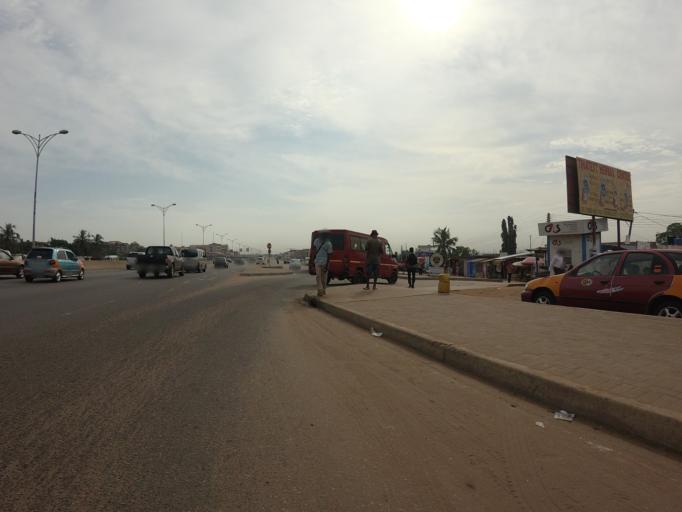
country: GH
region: Greater Accra
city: Dome
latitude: 5.6080
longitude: -0.2449
